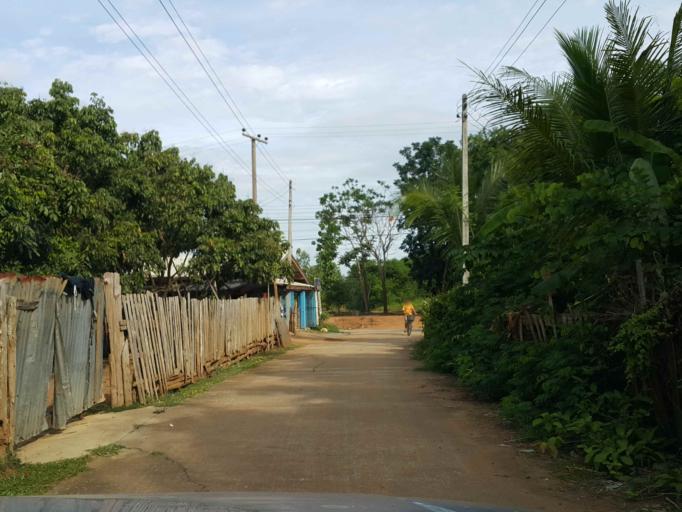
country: TH
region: Sukhothai
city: Thung Saliam
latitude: 17.3287
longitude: 99.4558
